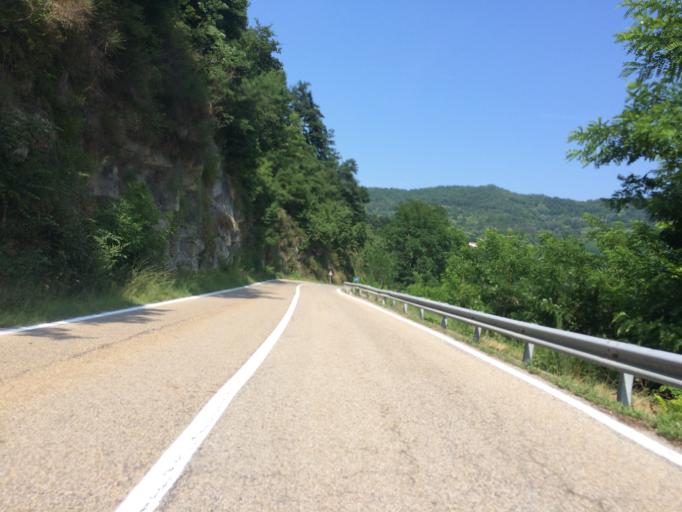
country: IT
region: Piedmont
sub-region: Provincia di Cuneo
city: Torre Bormida
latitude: 44.5609
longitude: 8.1654
